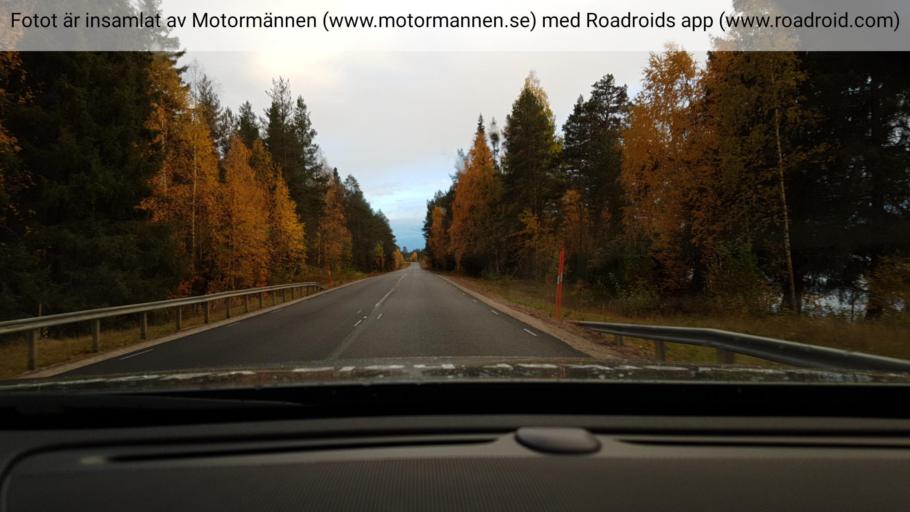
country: SE
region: Norrbotten
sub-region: Overkalix Kommun
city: OEverkalix
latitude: 66.4125
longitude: 22.8050
